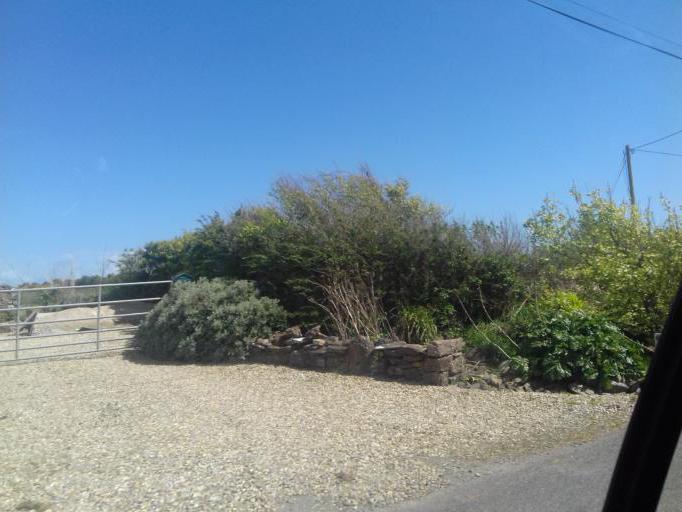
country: IE
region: Munster
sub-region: Waterford
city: Dunmore East
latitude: 52.1653
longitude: -6.8939
